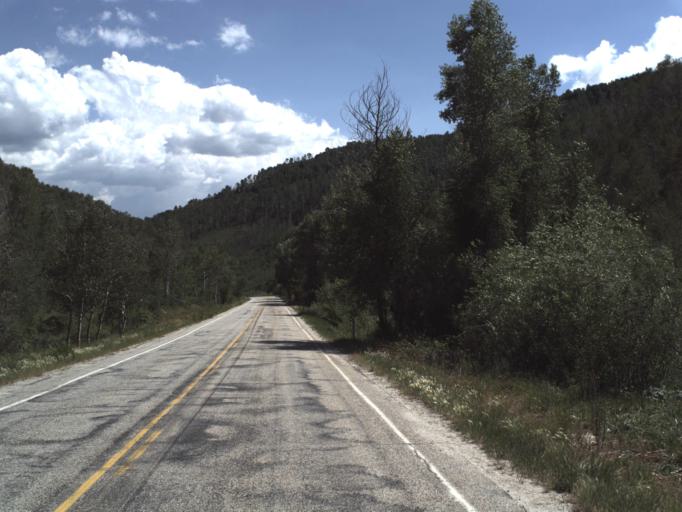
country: US
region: Utah
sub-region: Weber County
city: Wolf Creek
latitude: 41.4017
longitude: -111.5989
